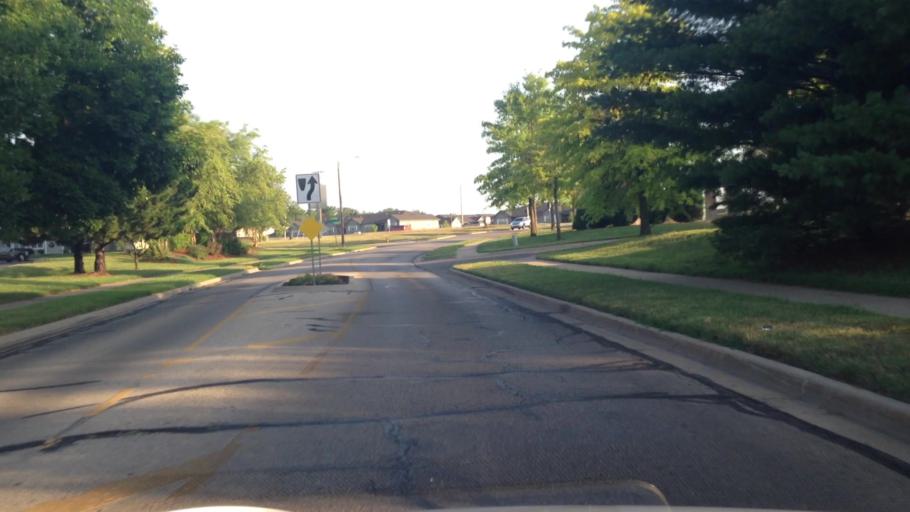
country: US
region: Kansas
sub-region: Douglas County
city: Lawrence
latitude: 38.9700
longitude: -95.3103
